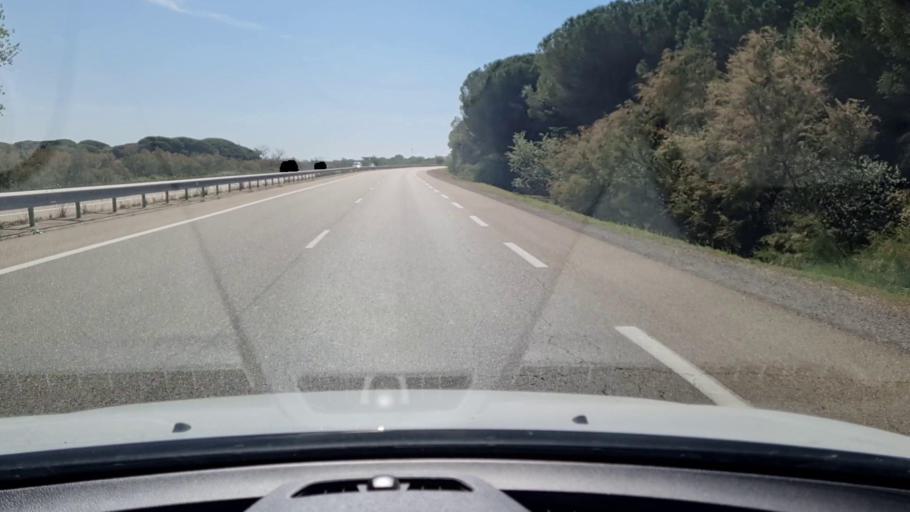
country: FR
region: Languedoc-Roussillon
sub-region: Departement du Gard
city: Le Grau-du-Roi
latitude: 43.5647
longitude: 4.1284
